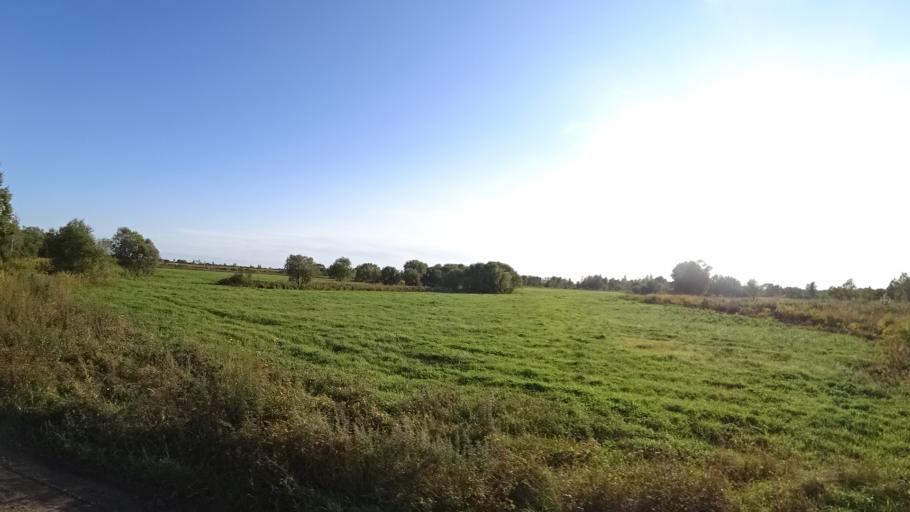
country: RU
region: Amur
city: Arkhara
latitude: 49.3545
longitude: 130.1341
